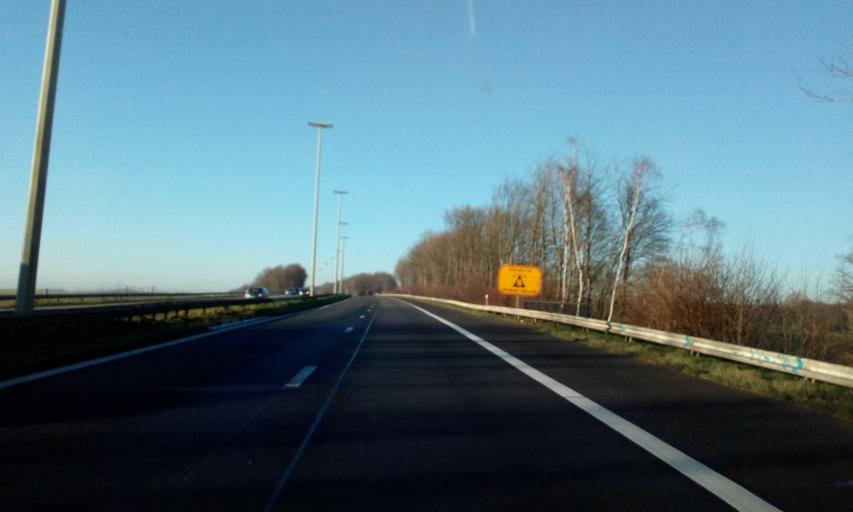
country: BE
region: Wallonia
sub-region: Province du Brabant Wallon
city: Nivelles
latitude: 50.5574
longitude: 4.3589
